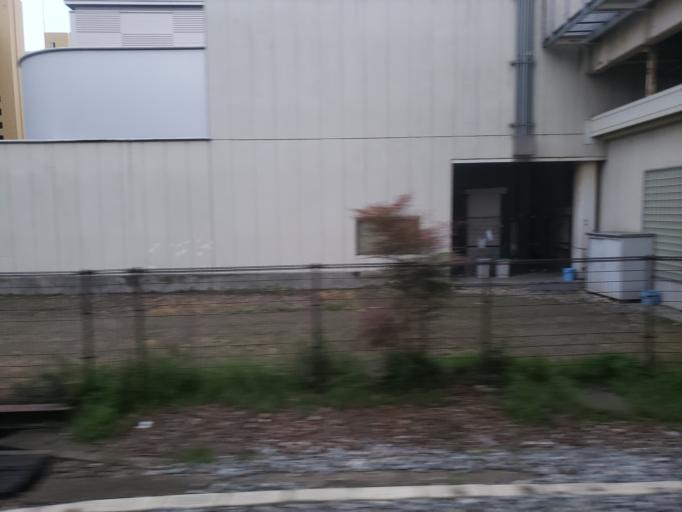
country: JP
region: Hyogo
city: Akashi
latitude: 34.6820
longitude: 134.9387
